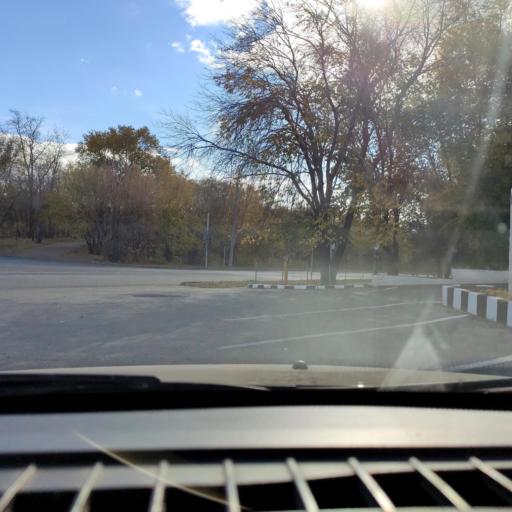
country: RU
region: Samara
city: Tol'yatti
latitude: 53.5057
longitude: 49.2543
